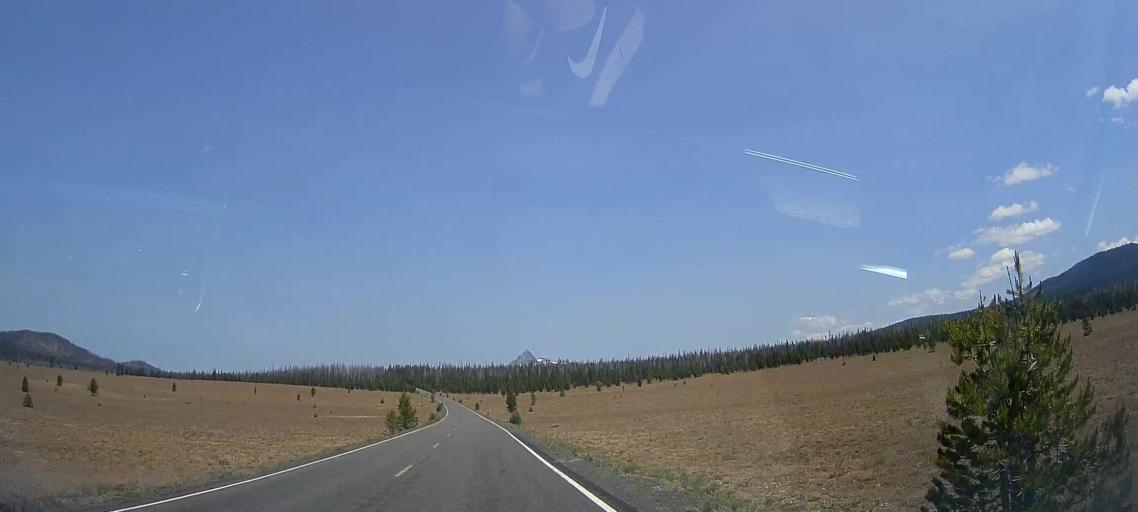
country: US
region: Oregon
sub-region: Lane County
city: Oakridge
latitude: 43.0299
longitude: -122.1183
